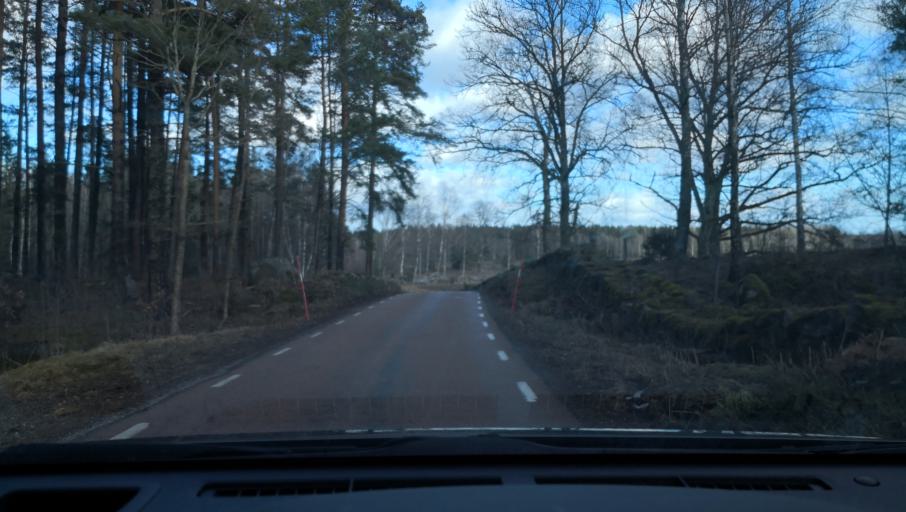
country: SE
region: Vaestmanland
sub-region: Arboga Kommun
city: Arboga
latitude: 59.3172
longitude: 15.7701
